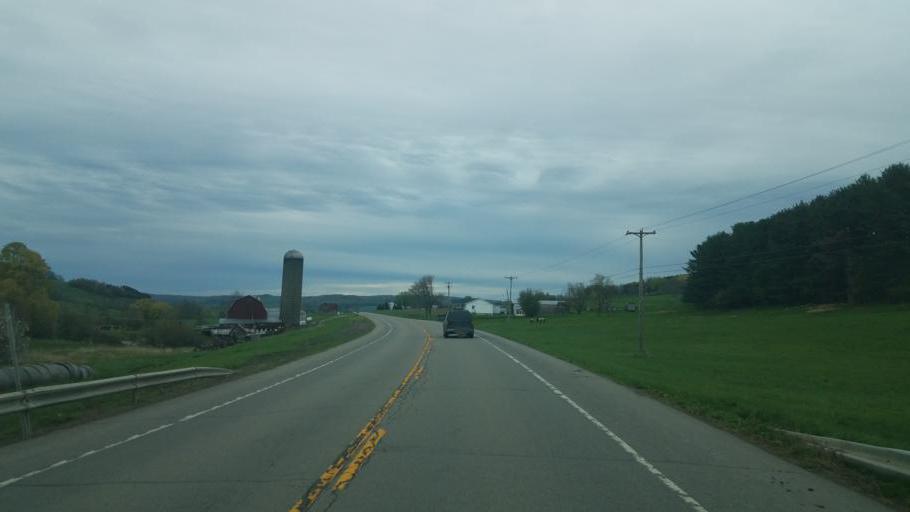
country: US
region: New York
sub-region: Steuben County
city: Canisteo
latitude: 42.1535
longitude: -77.5198
